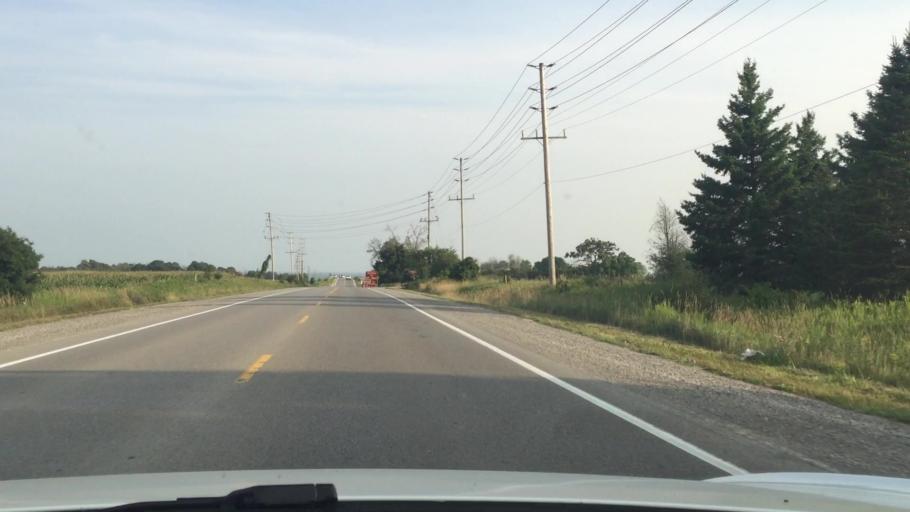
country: CA
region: Ontario
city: Oshawa
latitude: 43.8881
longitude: -78.7677
